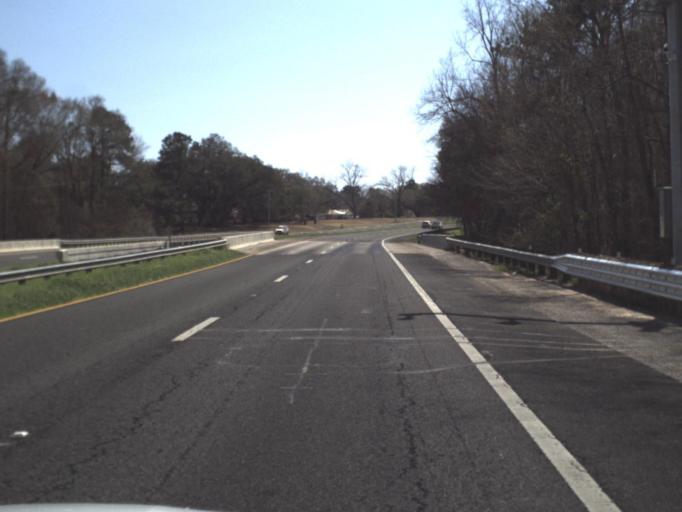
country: US
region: Florida
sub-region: Jackson County
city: Graceville
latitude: 30.9860
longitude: -85.4075
